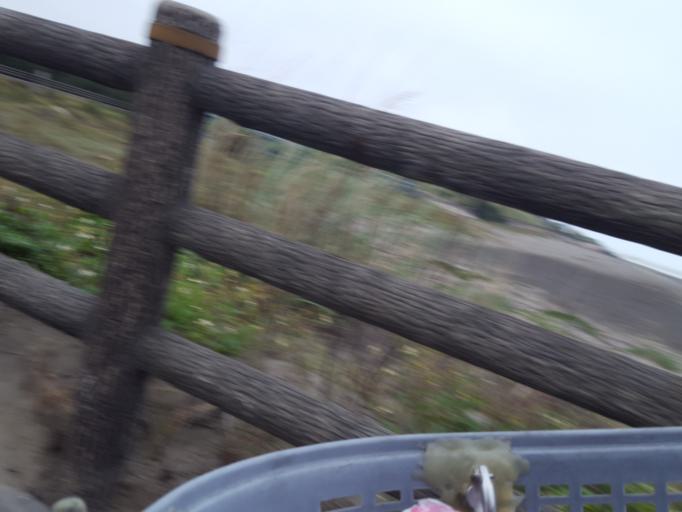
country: TW
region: Taiwan
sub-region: Hsinchu
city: Hsinchu
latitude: 24.8398
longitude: 120.9190
